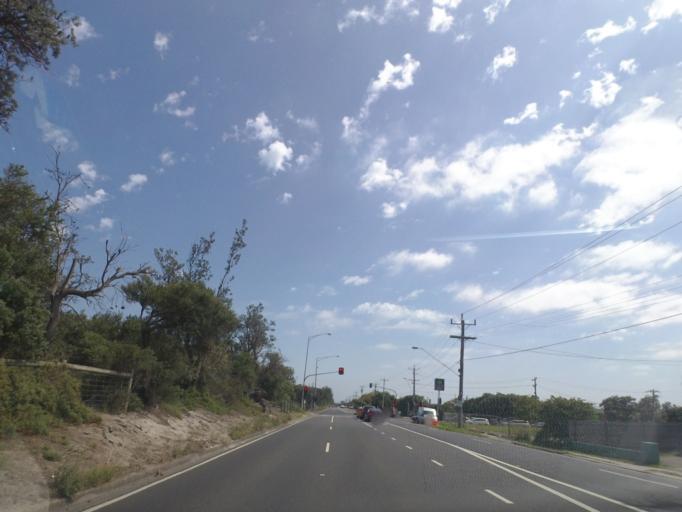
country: AU
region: Victoria
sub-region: Frankston
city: Seaford
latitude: -38.1105
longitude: 145.1257
